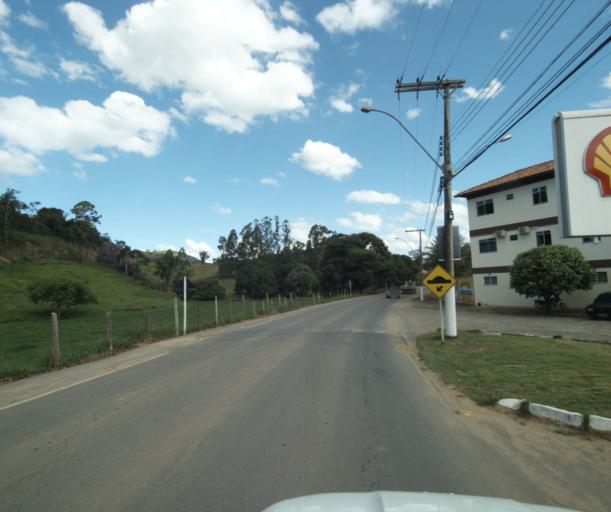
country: BR
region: Espirito Santo
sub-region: Sao Jose Do Calcado
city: Sao Jose do Calcado
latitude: -21.0340
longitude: -41.6520
